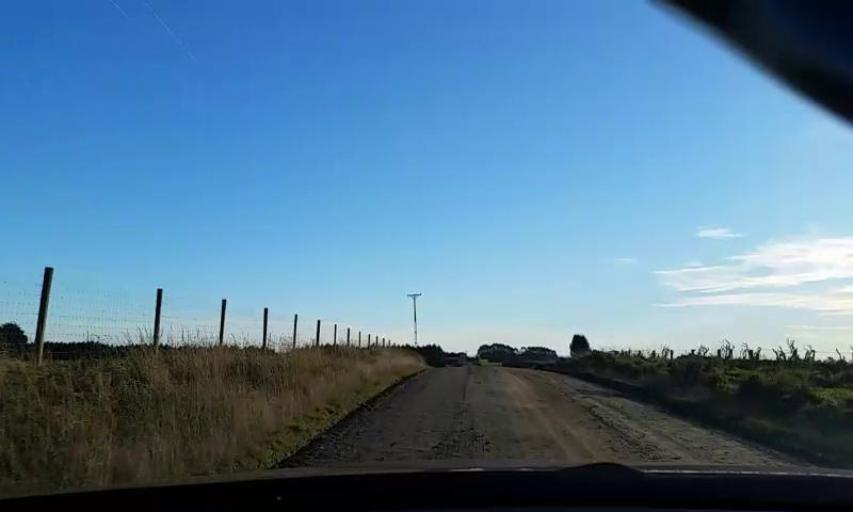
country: NZ
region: Southland
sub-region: Invercargill City
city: Invercargill
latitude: -46.2851
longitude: 168.4867
